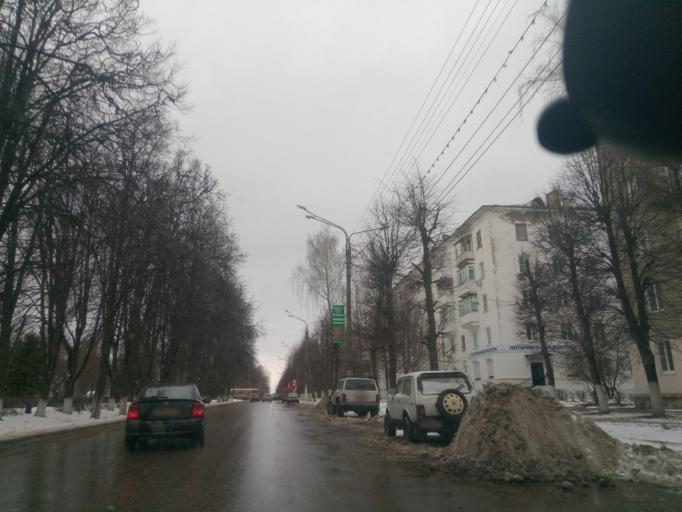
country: RU
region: Tula
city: Novomoskovsk
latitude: 54.0059
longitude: 38.2968
